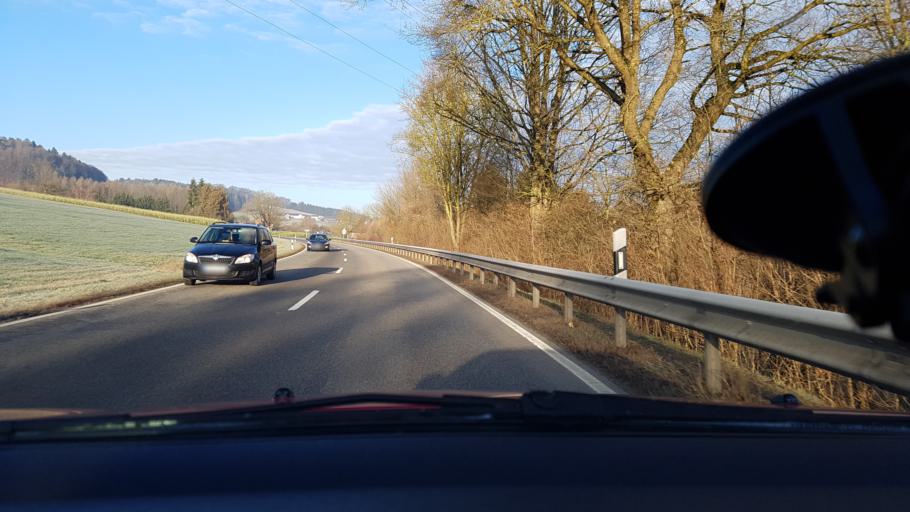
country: DE
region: Bavaria
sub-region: Lower Bavaria
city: Simbach am Inn
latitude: 48.2765
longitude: 12.9998
